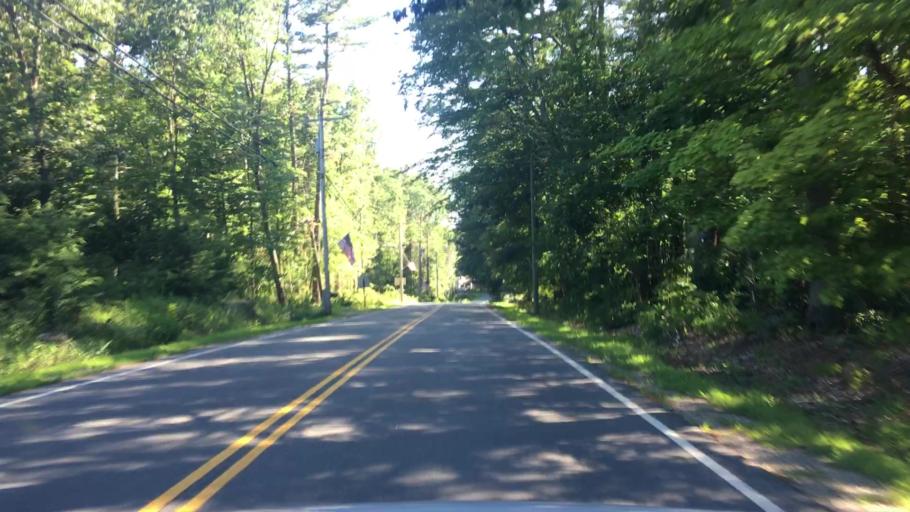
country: US
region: New Hampshire
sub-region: Rockingham County
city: Brentwood
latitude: 42.9822
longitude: -71.0677
